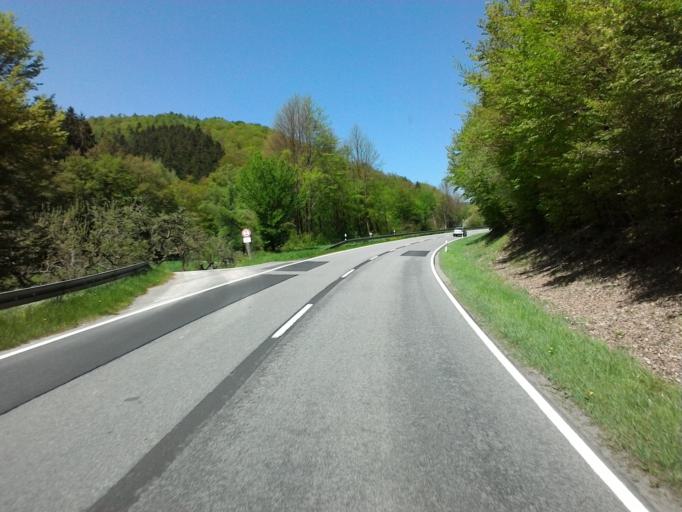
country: DE
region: Bavaria
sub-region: Regierungsbezirk Unterfranken
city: Rechtenbach
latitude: 49.9731
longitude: 9.5225
